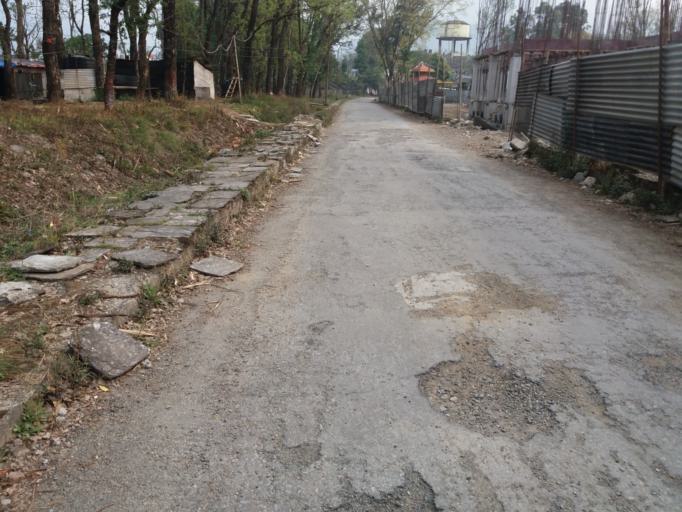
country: NP
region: Western Region
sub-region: Gandaki Zone
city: Pokhara
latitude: 28.2550
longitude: 83.9759
